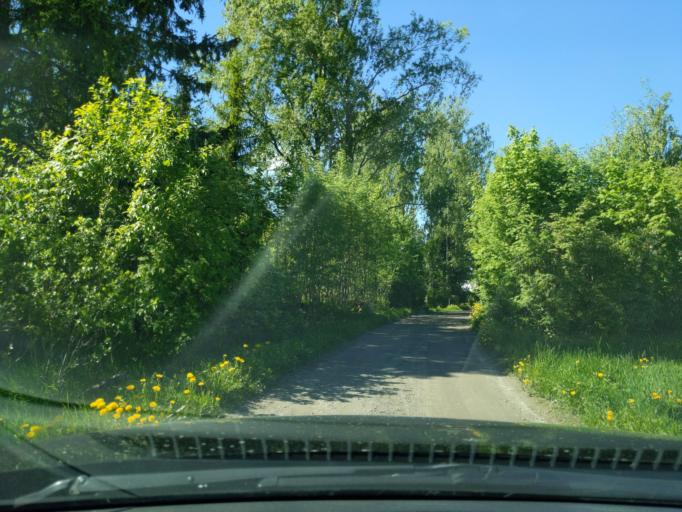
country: FI
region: Paijanne Tavastia
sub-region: Lahti
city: Lahti
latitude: 61.0594
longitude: 25.6638
